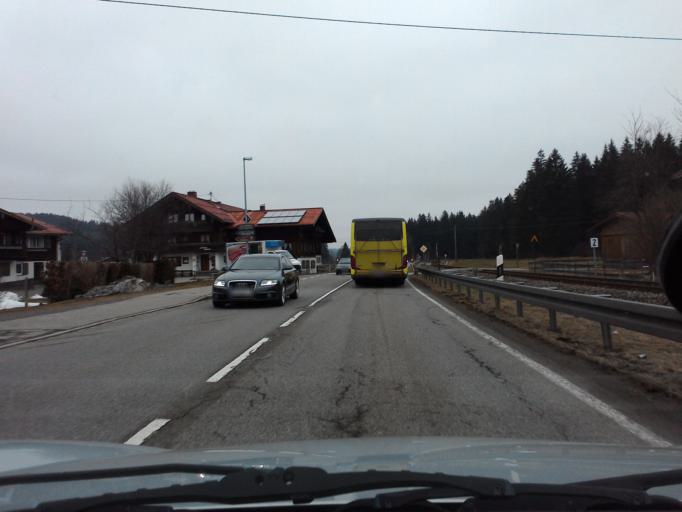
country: DE
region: Bavaria
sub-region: Swabia
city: Oberstdorf
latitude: 47.4393
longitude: 10.2757
